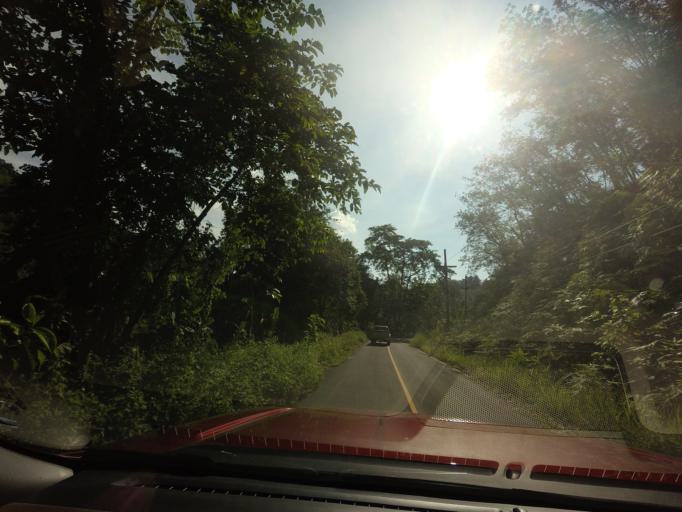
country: TH
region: Narathiwat
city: Si Sakhon
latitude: 6.0622
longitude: 101.3868
